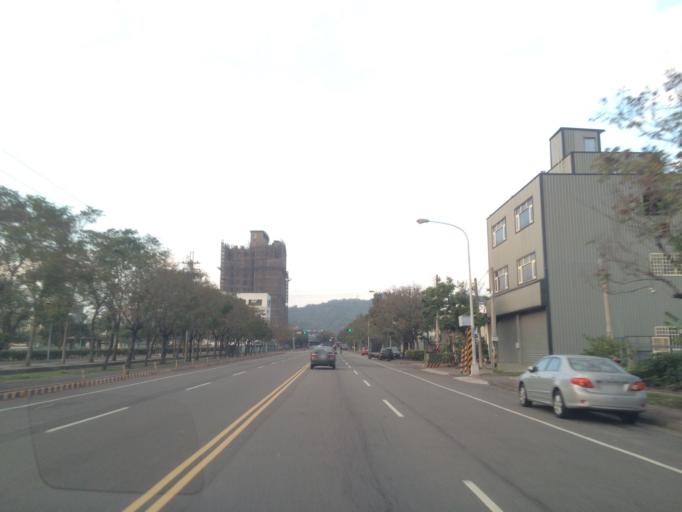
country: TW
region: Taiwan
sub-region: Taichung City
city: Taichung
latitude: 24.1674
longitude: 120.7334
